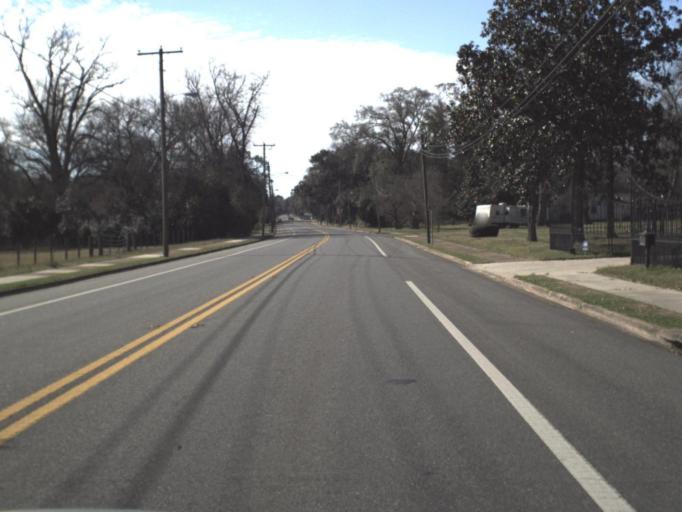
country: US
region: Florida
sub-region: Jackson County
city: Malone
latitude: 30.8755
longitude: -85.1618
